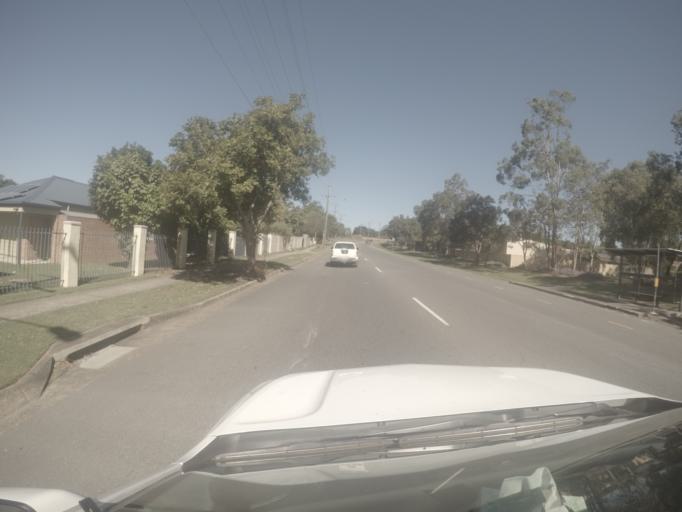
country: AU
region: Queensland
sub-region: Ipswich
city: Springfield
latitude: -27.6422
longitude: 152.9183
